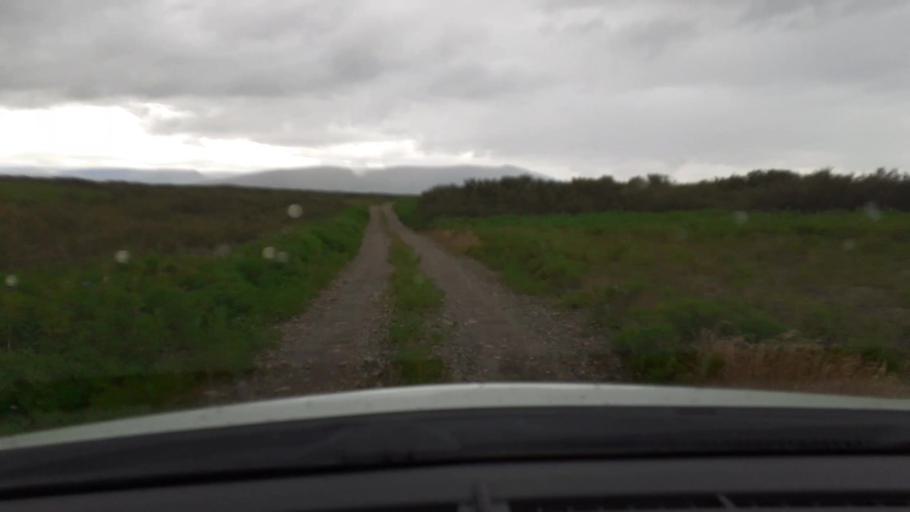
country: IS
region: West
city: Borgarnes
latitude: 64.4561
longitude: -21.9519
